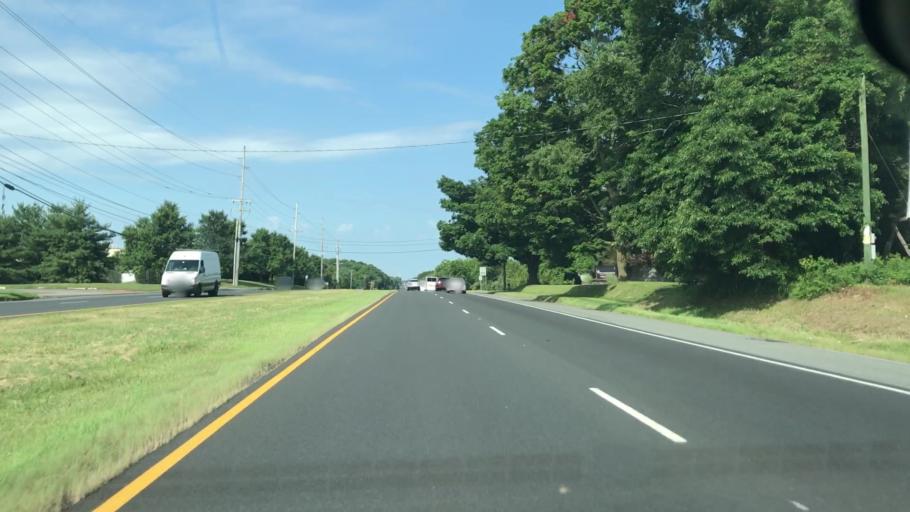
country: US
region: New Jersey
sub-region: Somerset County
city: Bradley Gardens
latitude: 40.5584
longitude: -74.7100
